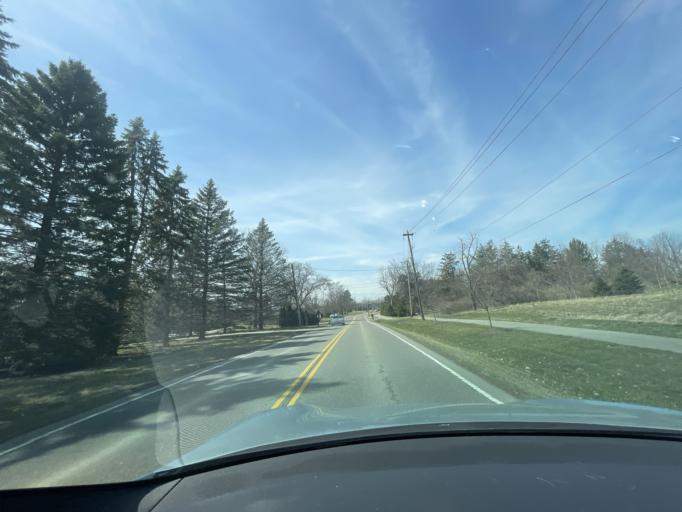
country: US
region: Ohio
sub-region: Franklin County
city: Dublin
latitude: 40.1179
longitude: -83.1287
